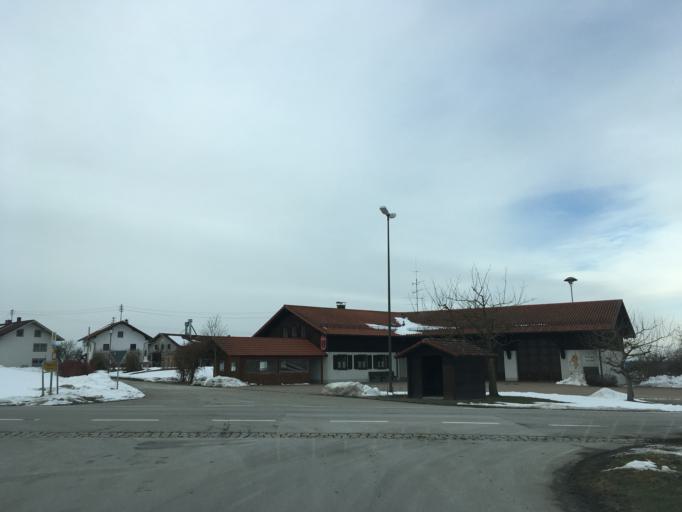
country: DE
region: Bavaria
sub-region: Upper Bavaria
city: Jettenbach
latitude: 48.1397
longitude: 12.3884
